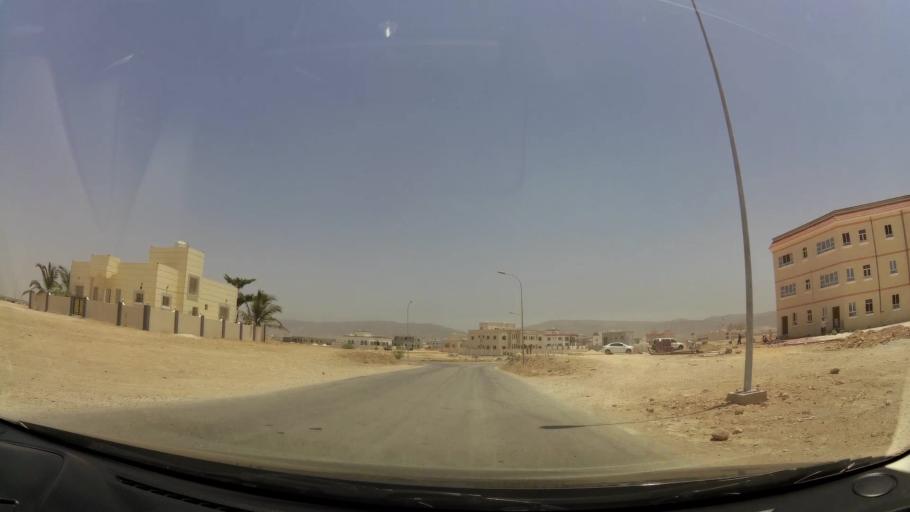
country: OM
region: Zufar
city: Salalah
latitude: 17.0967
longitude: 54.1704
